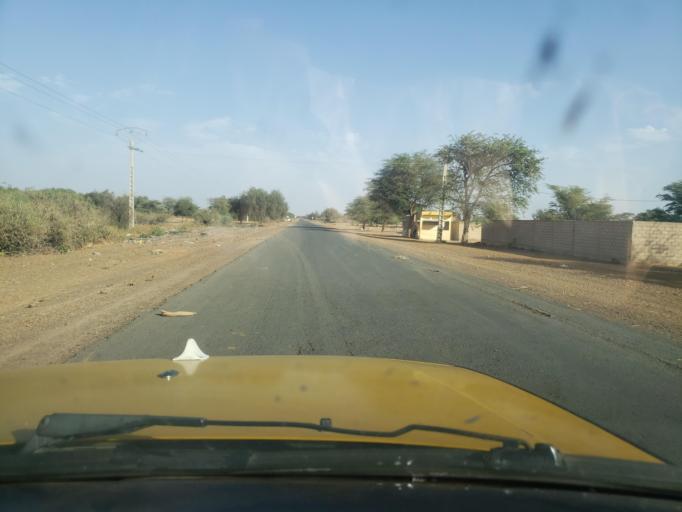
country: SN
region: Louga
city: Louga
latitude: 15.5014
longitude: -15.9400
